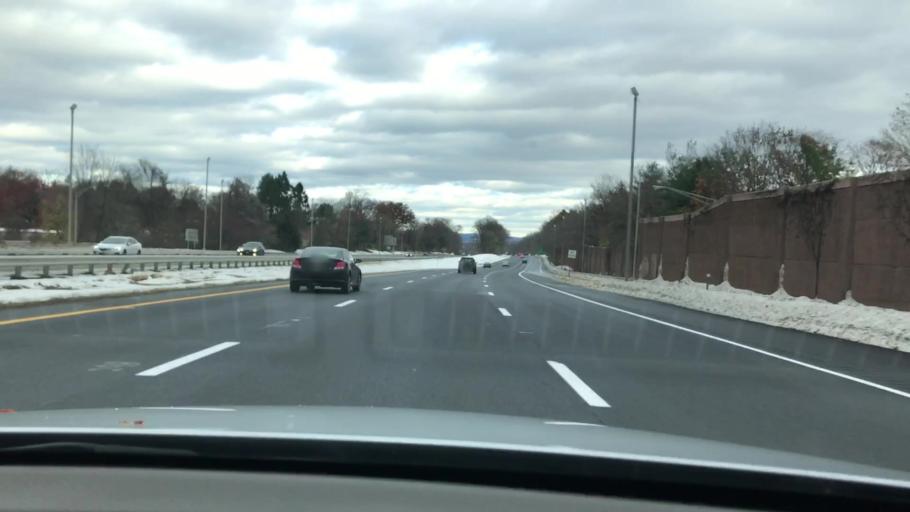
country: US
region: New Jersey
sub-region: Morris County
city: Boonton
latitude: 40.9085
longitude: -74.3933
